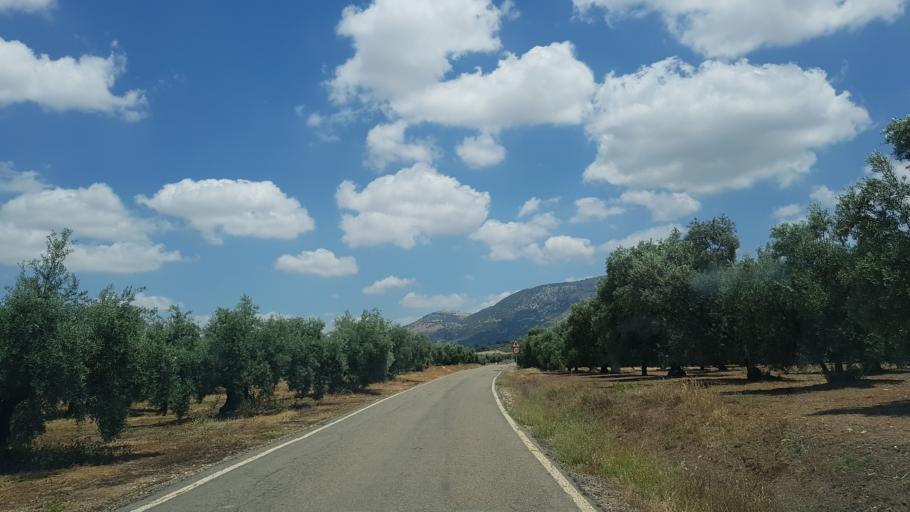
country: ES
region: Andalusia
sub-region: Province of Cordoba
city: Cabra
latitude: 37.5180
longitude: -4.4473
